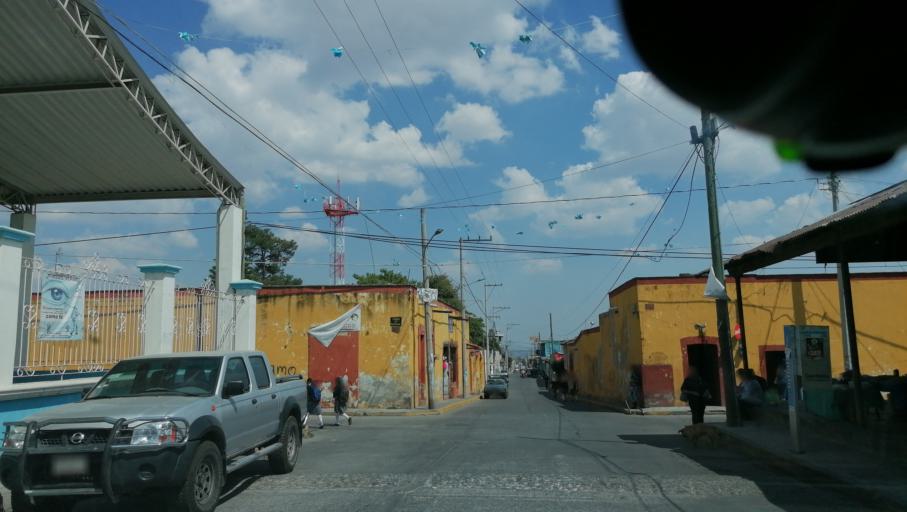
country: MX
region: Puebla
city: San Andres Calpan
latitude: 19.1052
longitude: -98.4636
